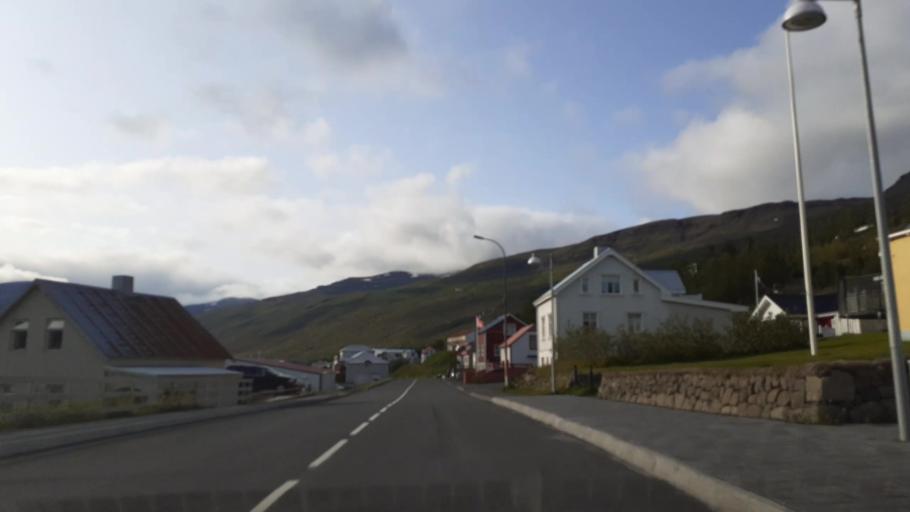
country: IS
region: East
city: Eskifjoerdur
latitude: 65.0675
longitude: -14.0055
